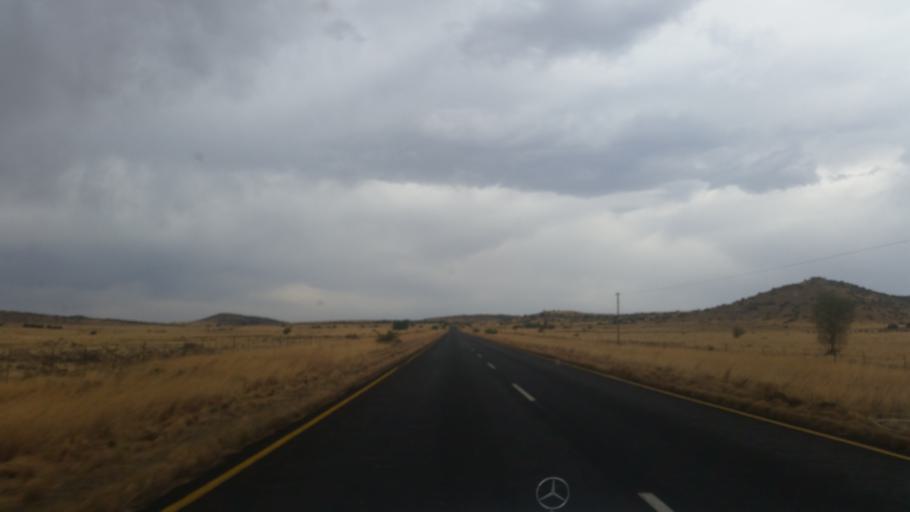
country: ZA
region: Eastern Cape
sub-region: Joe Gqabi District Municipality
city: Aliwal North
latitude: -30.4000
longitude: 26.2347
